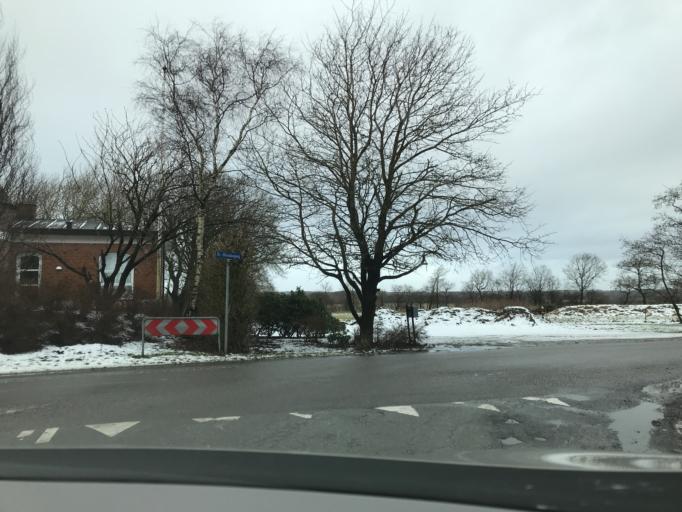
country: DK
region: South Denmark
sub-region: Varde Kommune
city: Varde
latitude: 55.6590
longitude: 8.4203
